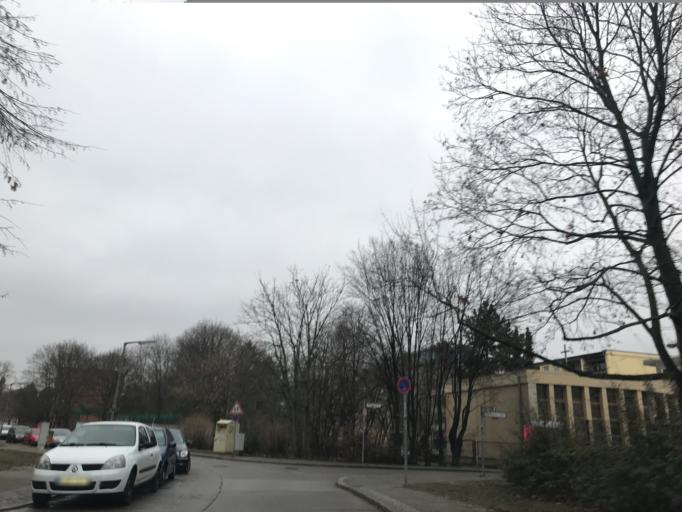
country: DE
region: Berlin
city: Spandau
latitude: 52.5492
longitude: 13.1838
